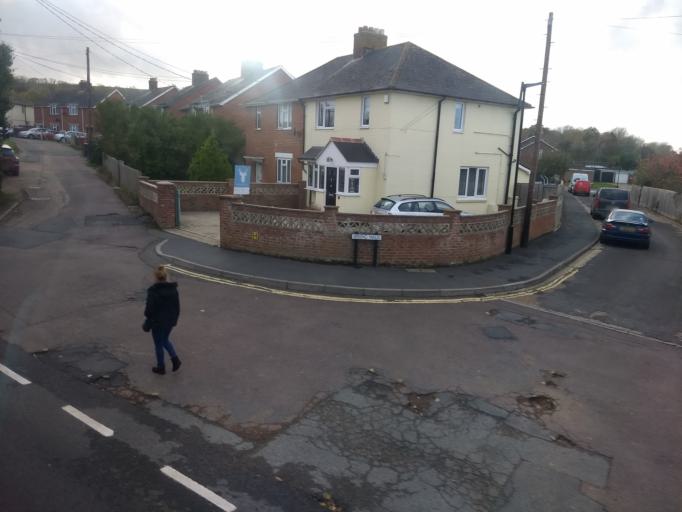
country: GB
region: England
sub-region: Isle of Wight
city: Newport
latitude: 50.6971
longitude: -1.3207
